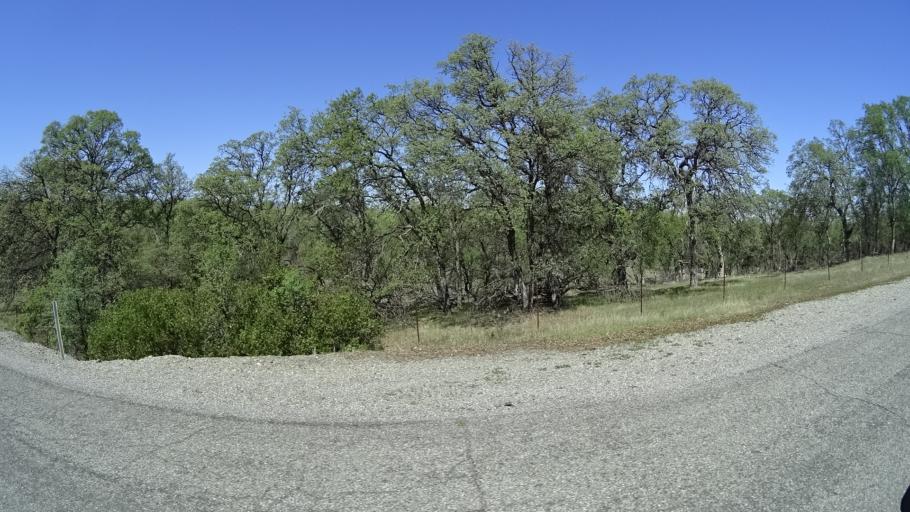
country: US
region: California
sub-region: Glenn County
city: Orland
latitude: 39.7403
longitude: -122.3881
